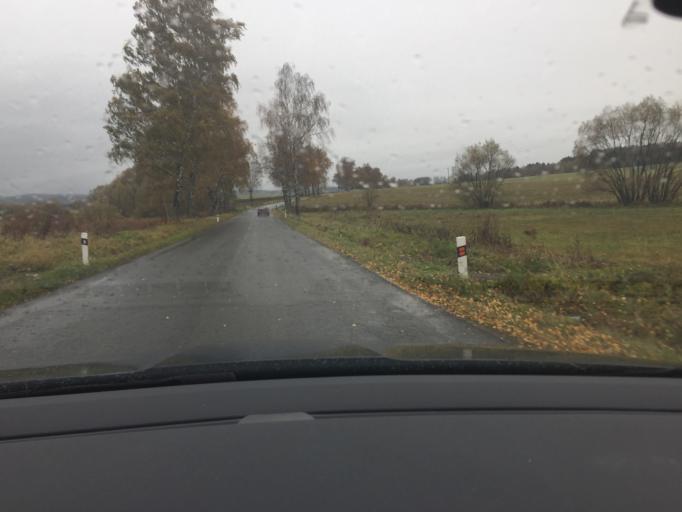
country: SK
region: Presovsky
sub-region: Okres Presov
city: Kezmarok
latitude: 49.1849
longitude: 20.3950
